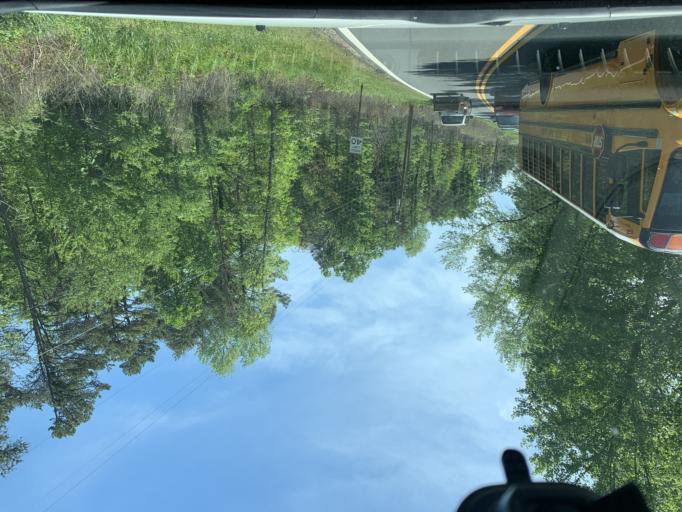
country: US
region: Georgia
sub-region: Forsyth County
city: Cumming
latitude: 34.2648
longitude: -84.0439
